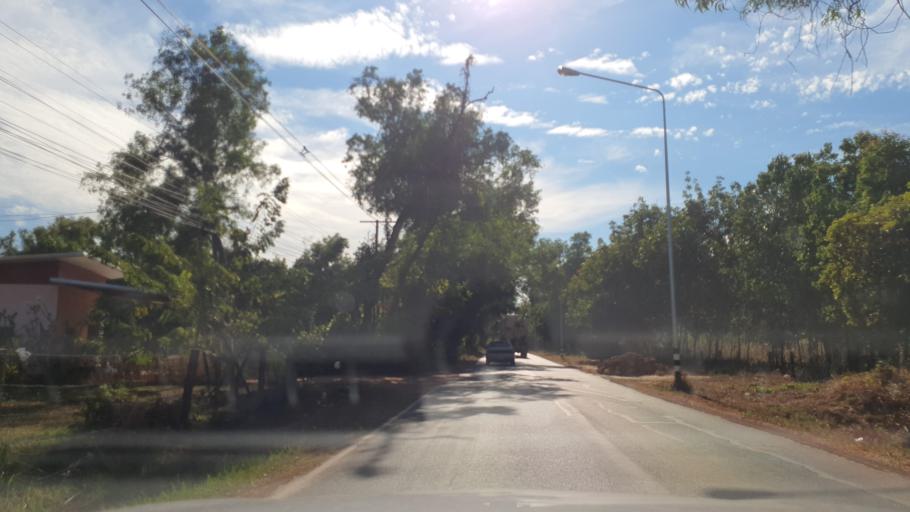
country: TH
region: Kalasin
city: Kuchinarai
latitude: 16.5387
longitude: 104.0785
